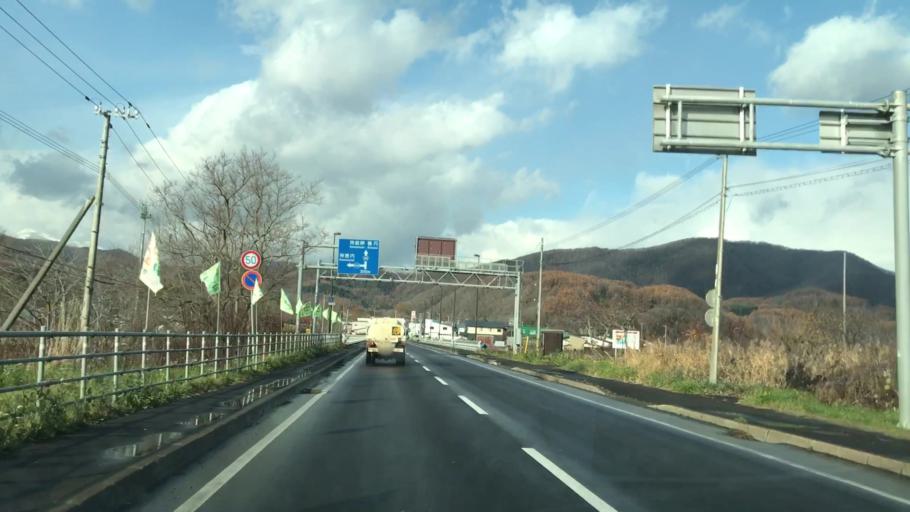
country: JP
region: Hokkaido
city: Yoichi
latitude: 43.2617
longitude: 140.6474
